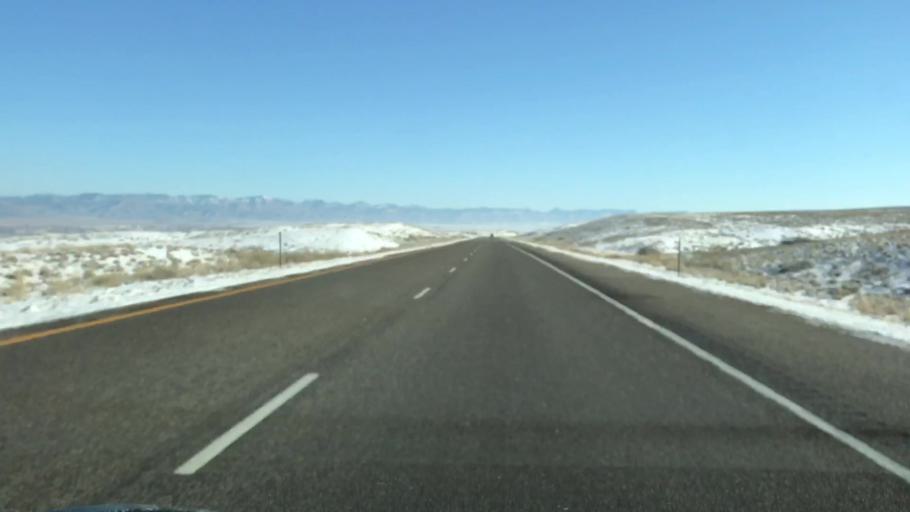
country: US
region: Colorado
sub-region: Mesa County
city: Loma
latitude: 39.2274
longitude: -108.9215
